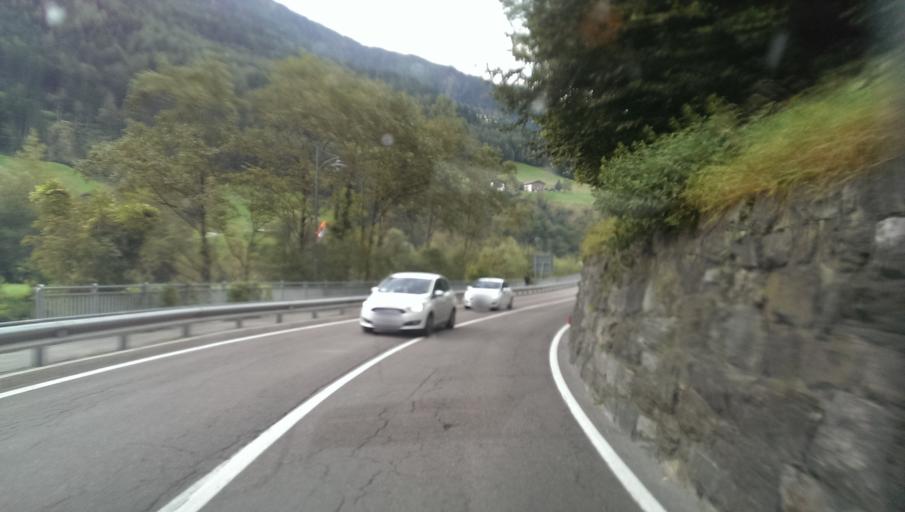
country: IT
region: Trentino-Alto Adige
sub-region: Bolzano
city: San Martino in Passiria
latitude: 46.7884
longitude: 11.2311
